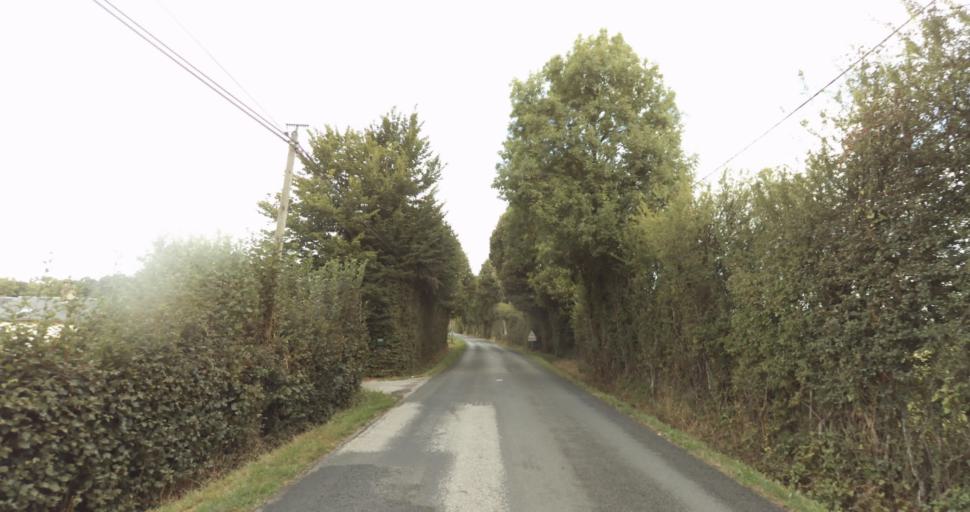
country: FR
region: Lower Normandy
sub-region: Departement de l'Orne
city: Gace
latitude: 48.7962
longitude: 0.2595
